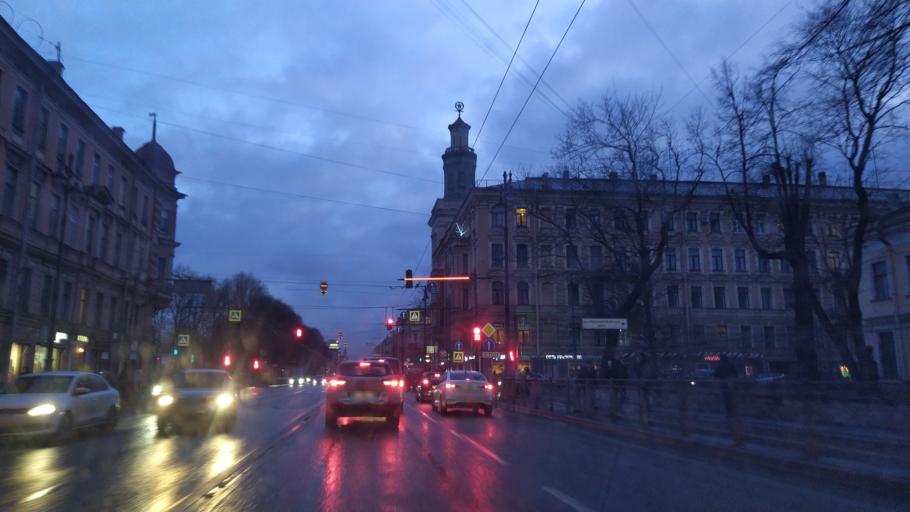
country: RU
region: St.-Petersburg
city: Saint Petersburg
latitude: 59.9143
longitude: 30.3181
